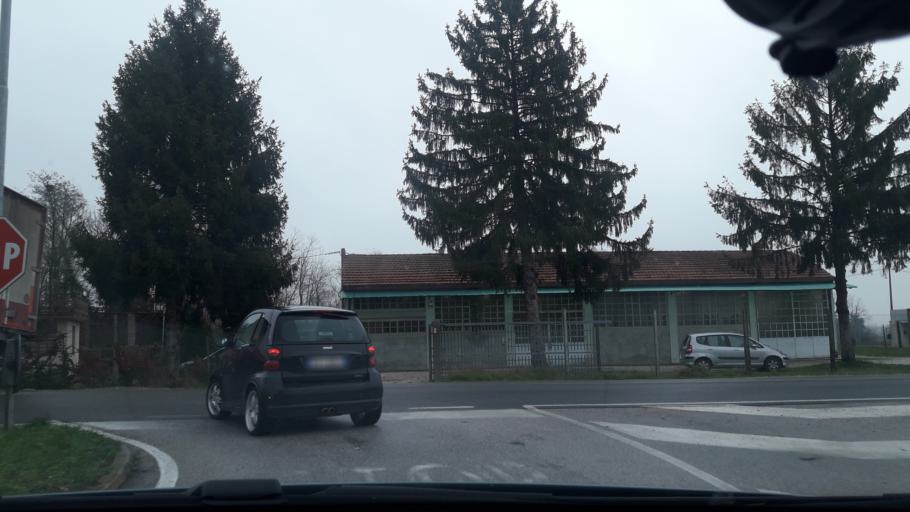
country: IT
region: Friuli Venezia Giulia
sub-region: Provincia di Udine
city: Pozzuolo del Friuli
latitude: 45.9868
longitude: 13.2012
